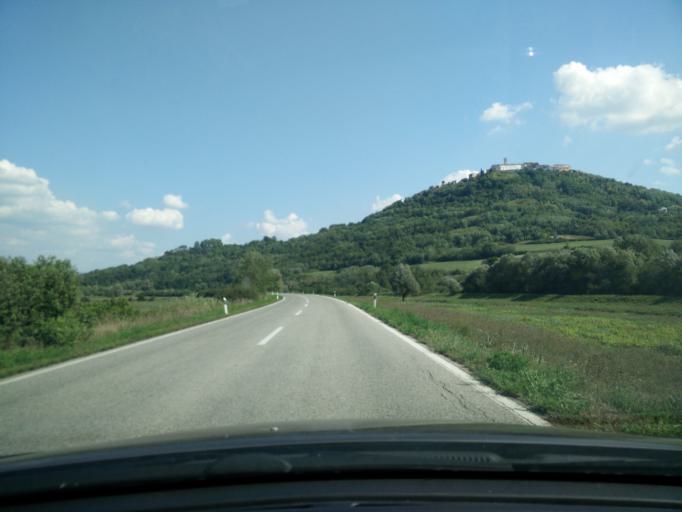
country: HR
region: Istarska
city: Karojba
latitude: 45.3433
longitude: 13.8151
